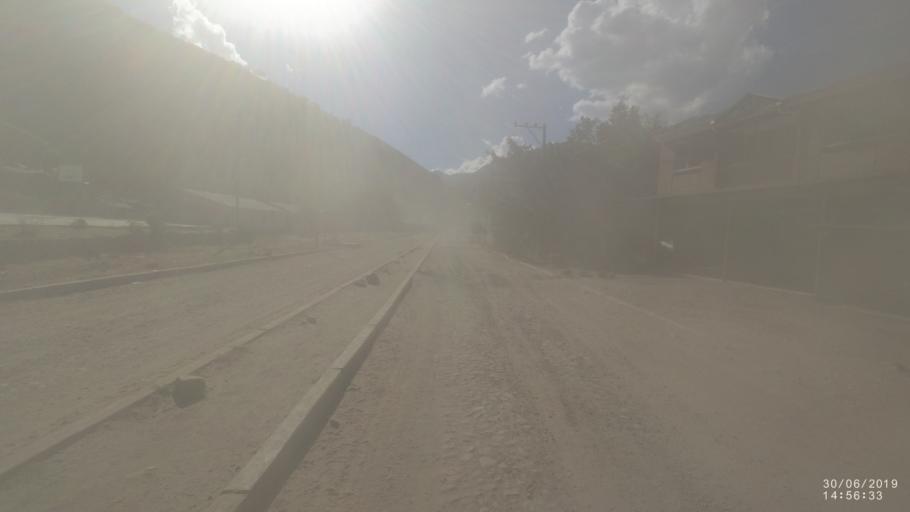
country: BO
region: Cochabamba
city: Irpa Irpa
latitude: -17.7486
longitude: -66.3537
